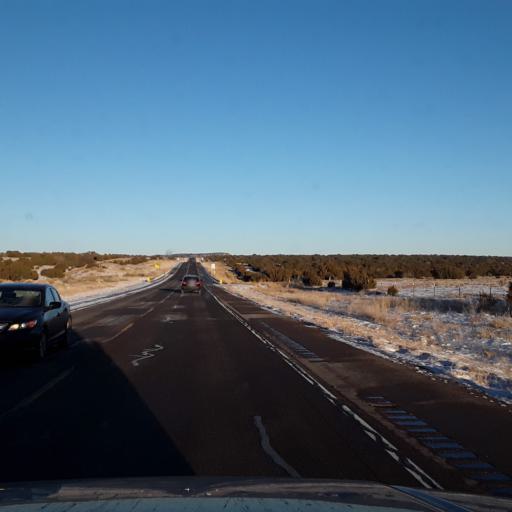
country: US
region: New Mexico
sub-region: Lincoln County
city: Carrizozo
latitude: 34.2306
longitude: -105.6291
